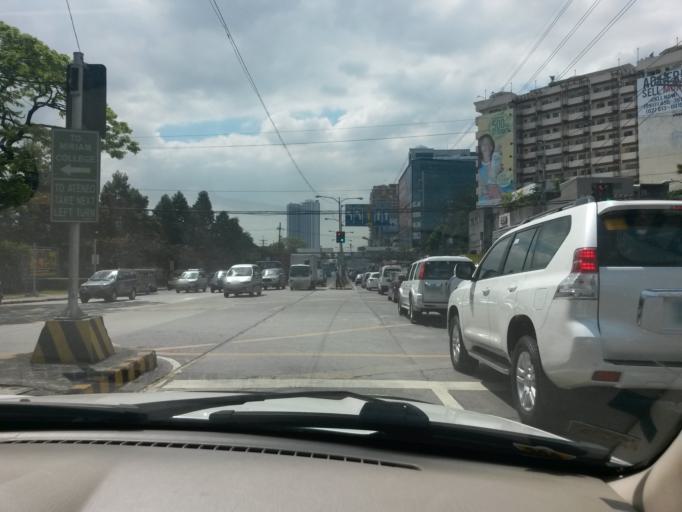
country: PH
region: Metro Manila
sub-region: Quezon City
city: Quezon City
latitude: 14.6428
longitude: 121.0746
